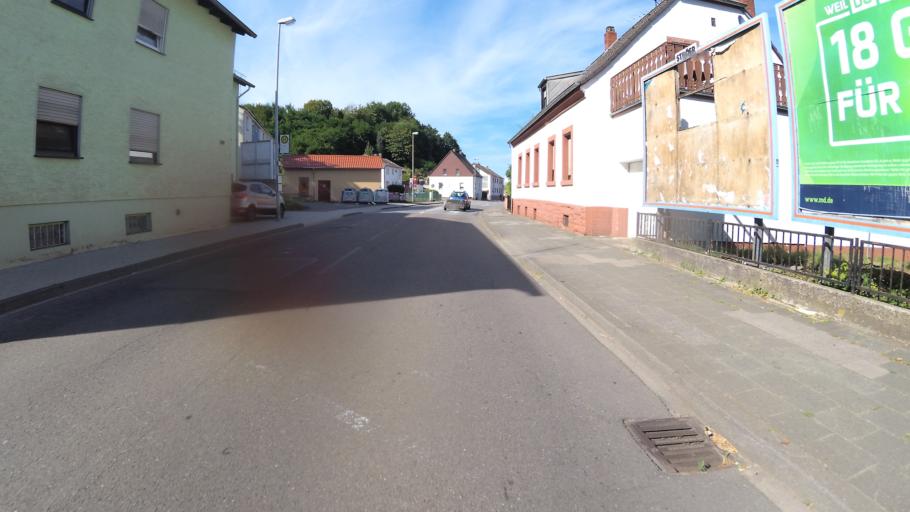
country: DE
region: Rheinland-Pfalz
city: Zweibrucken
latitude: 49.2315
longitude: 7.3541
